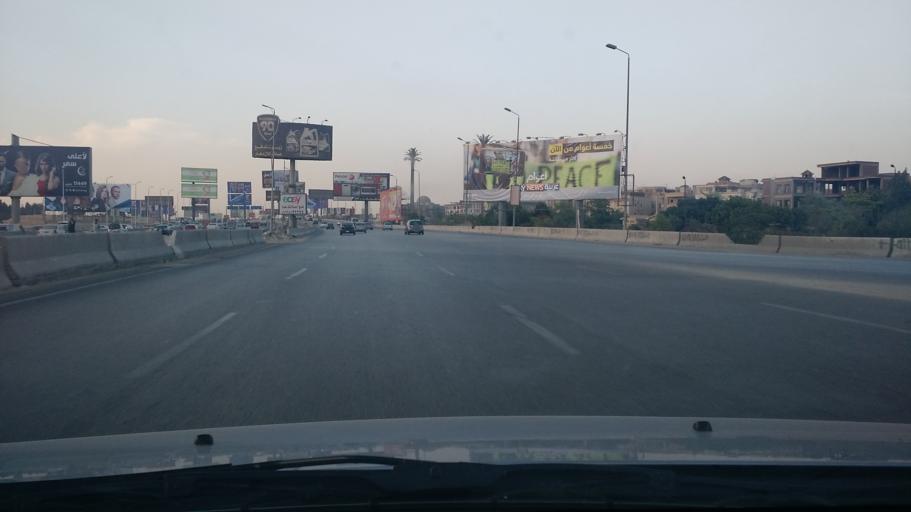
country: EG
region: Muhafazat al Qahirah
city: Cairo
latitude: 30.0011
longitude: 31.3968
